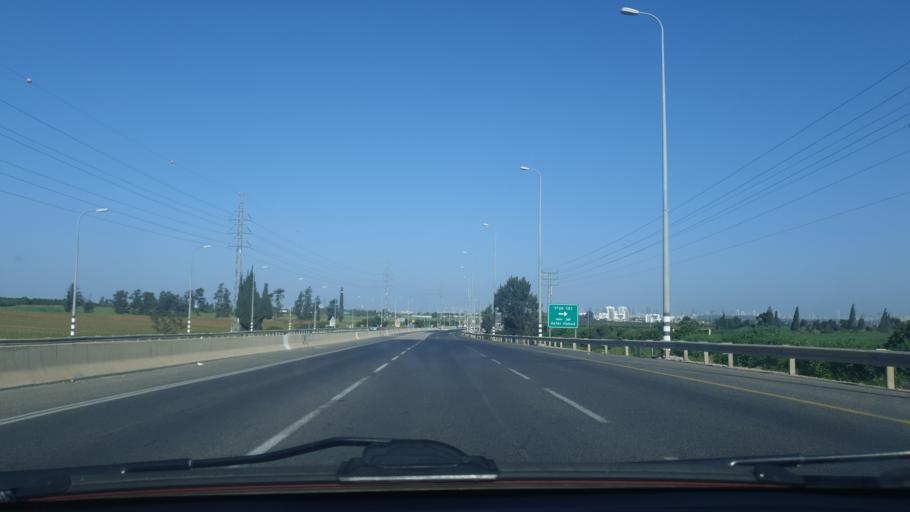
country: IL
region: Central District
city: Kefar Habad
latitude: 31.9763
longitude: 34.8390
